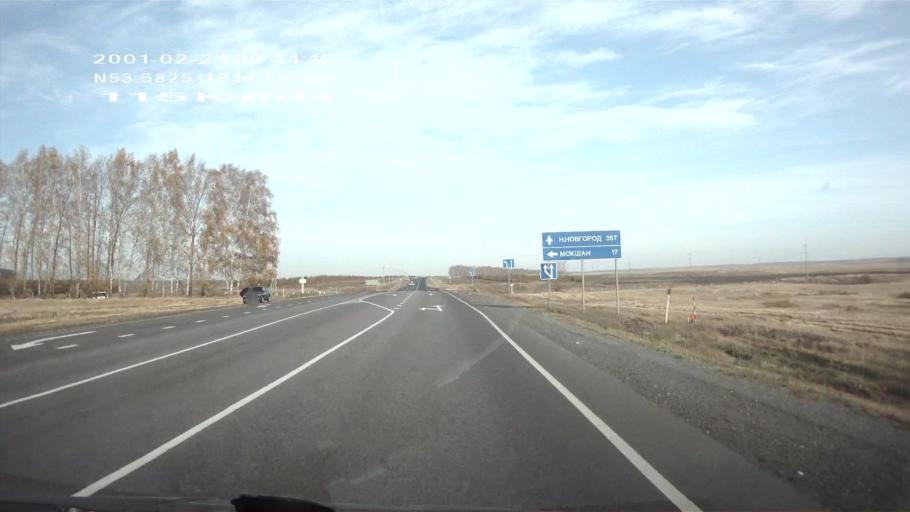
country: RU
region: Penza
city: Mokshan
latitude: 53.5829
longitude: 44.7276
